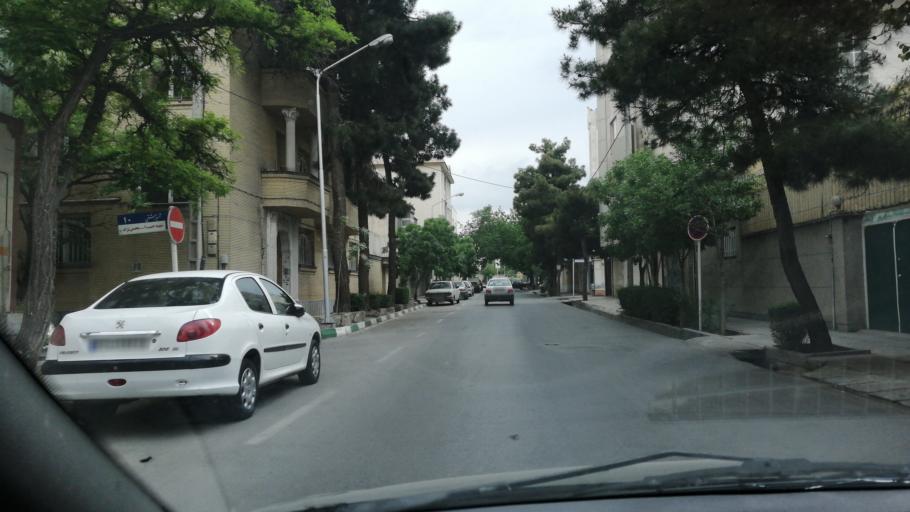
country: IR
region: Razavi Khorasan
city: Mashhad
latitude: 36.2870
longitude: 59.5839
